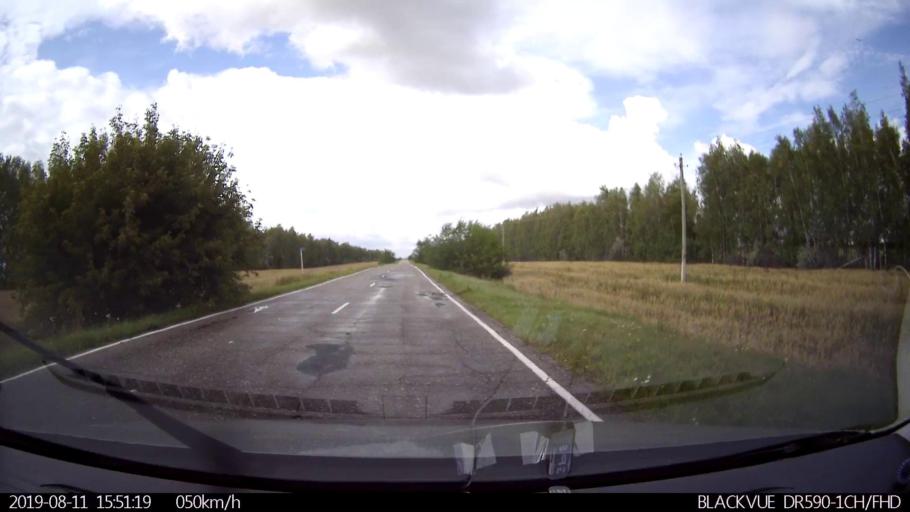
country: RU
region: Ulyanovsk
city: Ignatovka
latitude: 53.9180
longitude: 47.6560
